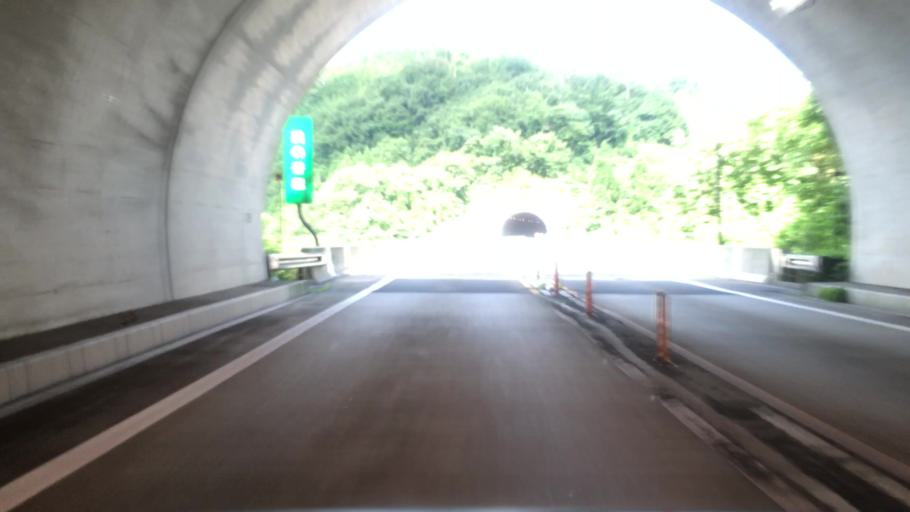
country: JP
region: Hyogo
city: Toyooka
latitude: 35.6284
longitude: 134.6087
